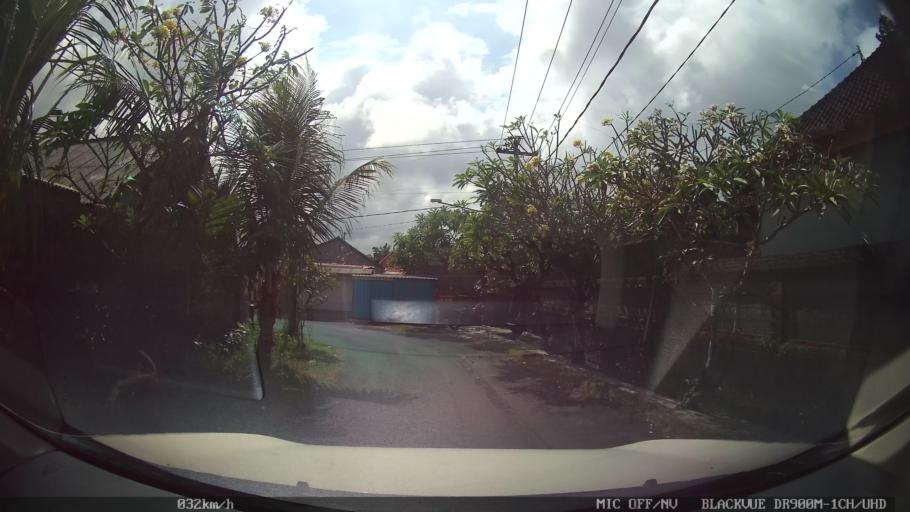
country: ID
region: Bali
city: Banjar Batur
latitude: -8.5978
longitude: 115.2093
